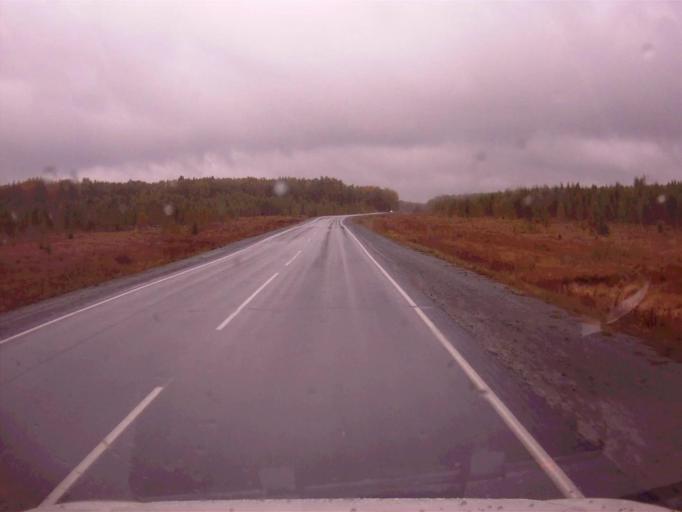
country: RU
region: Chelyabinsk
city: Tayginka
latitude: 55.5052
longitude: 60.6367
